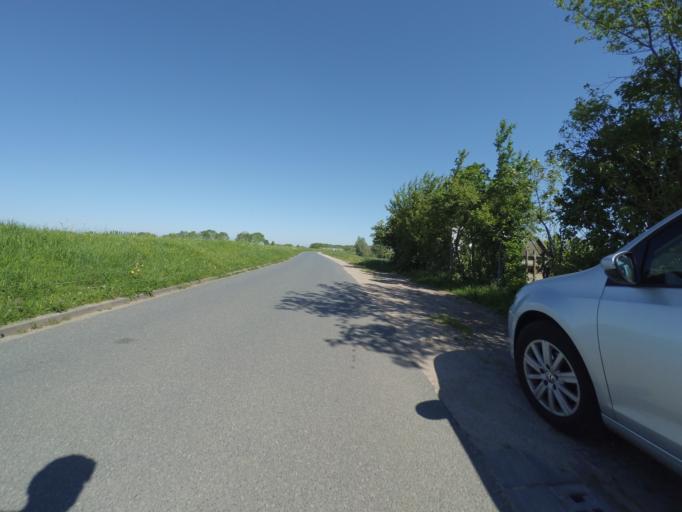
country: NL
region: Gelderland
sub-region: Gemeente Zutphen
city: Zutphen
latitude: 52.1466
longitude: 6.1829
